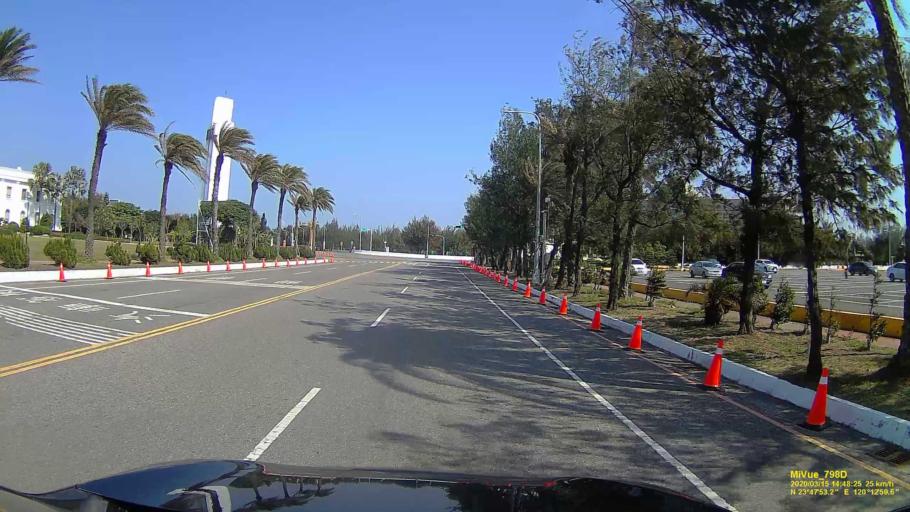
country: TW
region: Taiwan
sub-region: Yunlin
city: Douliu
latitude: 23.7981
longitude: 120.2168
